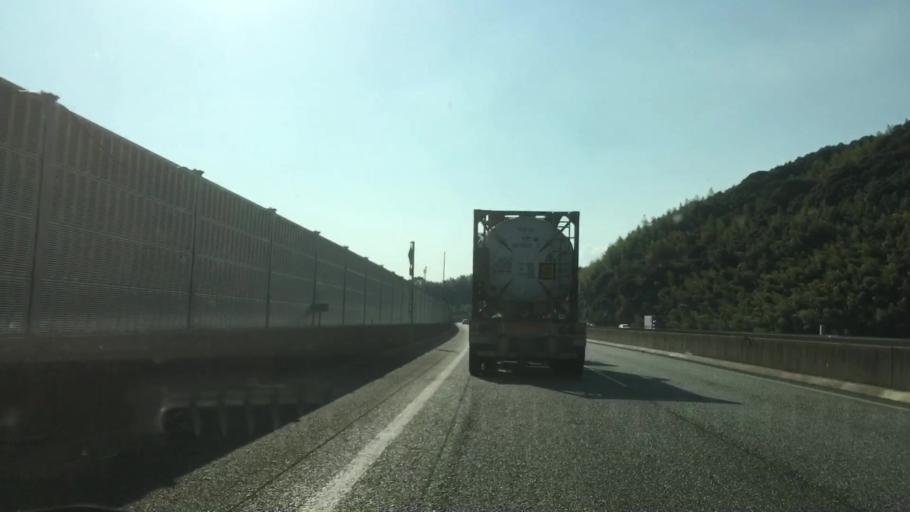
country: JP
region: Yamaguchi
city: Kudamatsu
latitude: 34.0444
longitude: 131.8680
